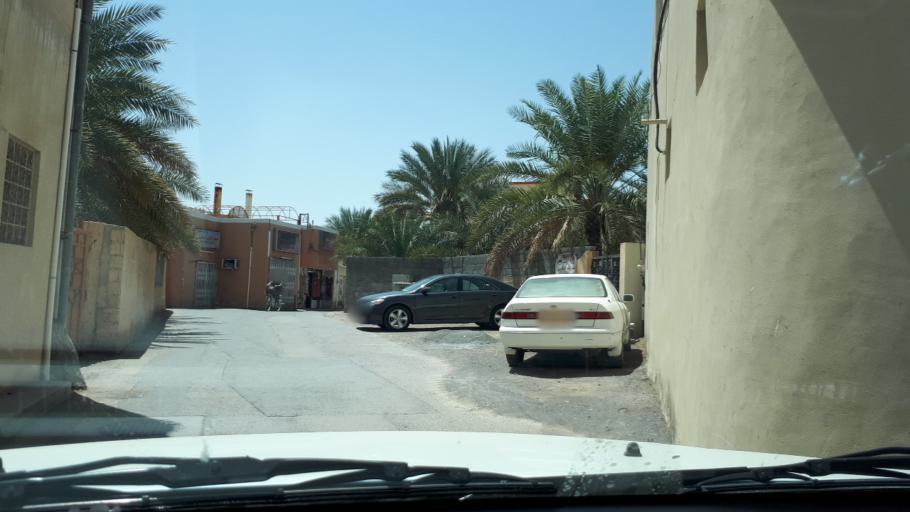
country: OM
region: Muhafazat ad Dakhiliyah
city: Nizwa
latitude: 22.9295
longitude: 57.5320
